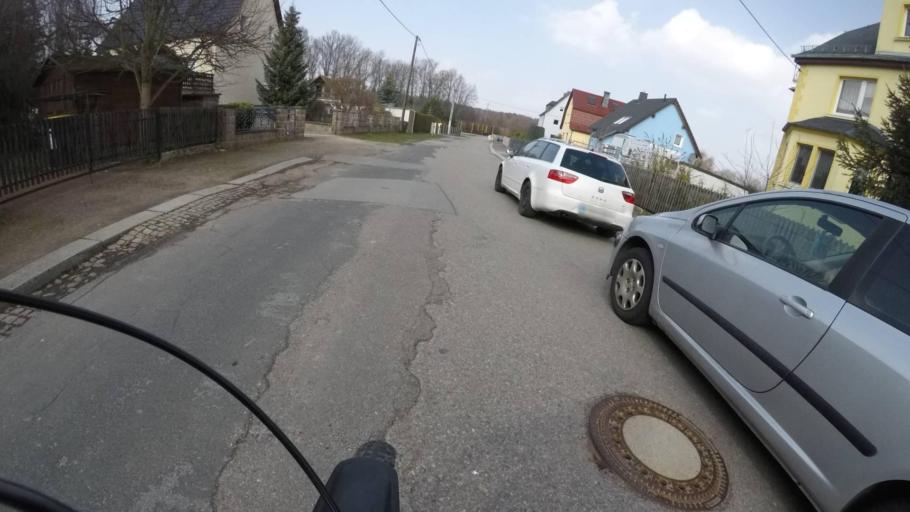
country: DE
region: Saxony
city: Limbach-Oberfrohna
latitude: 50.8603
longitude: 12.7948
